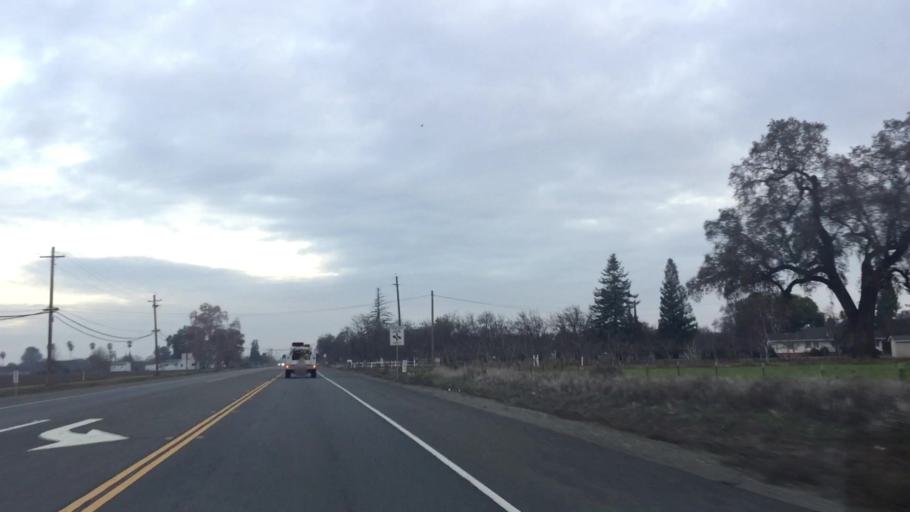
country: US
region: California
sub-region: Yuba County
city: Marysville
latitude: 39.2092
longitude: -121.5969
